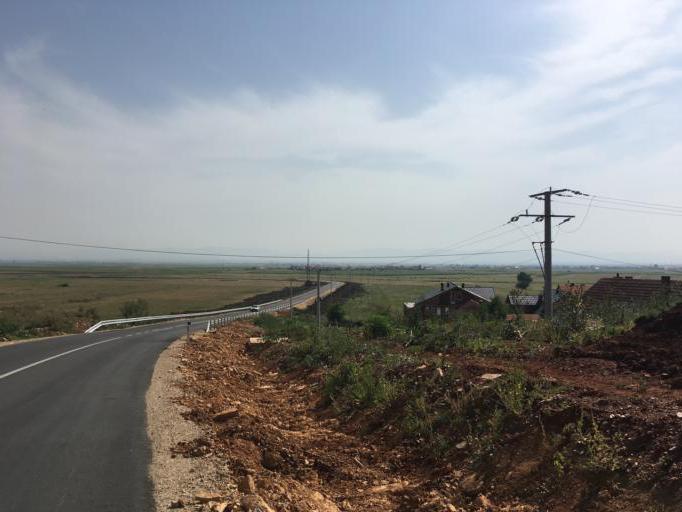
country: XK
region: Pristina
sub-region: Komuna e Gracanices
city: Glanica
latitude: 42.5431
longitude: 21.0149
